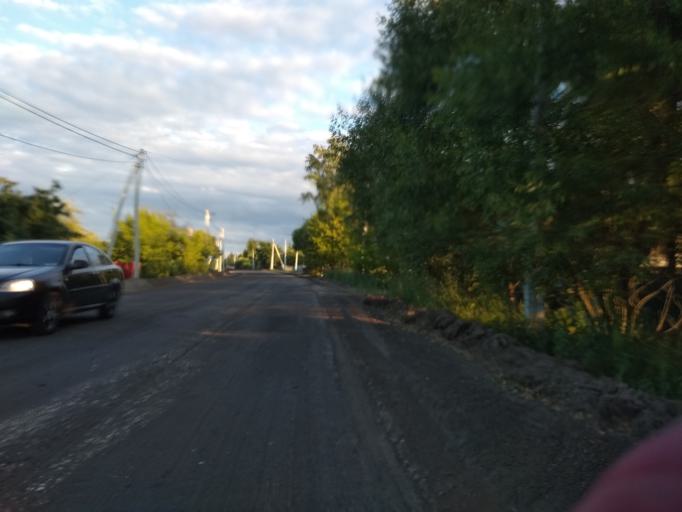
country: RU
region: Moskovskaya
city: Misheronskiy
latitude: 55.6553
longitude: 39.7522
